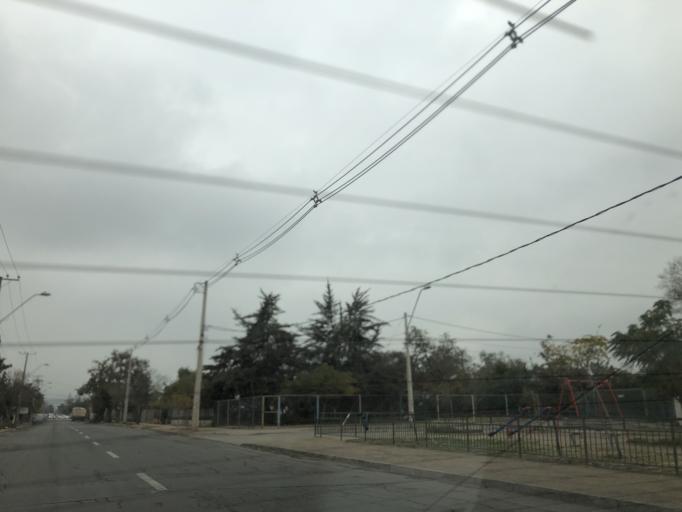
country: CL
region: Santiago Metropolitan
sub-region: Provincia de Santiago
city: La Pintana
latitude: -33.5849
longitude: -70.6067
